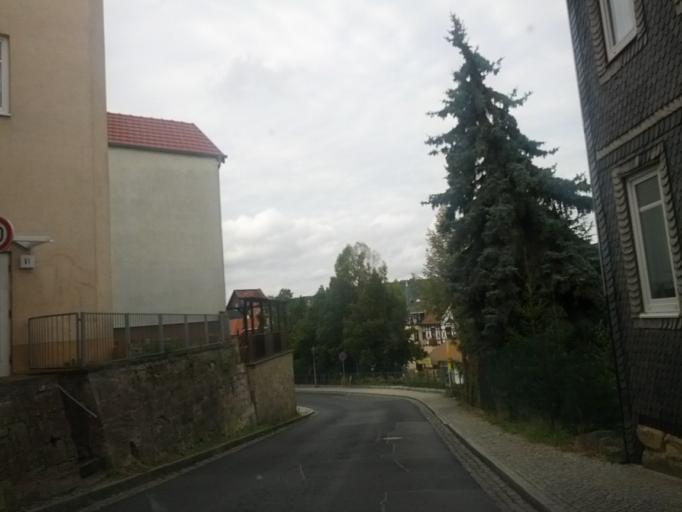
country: DE
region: Thuringia
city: Bad Salzungen
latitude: 50.8135
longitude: 10.2408
